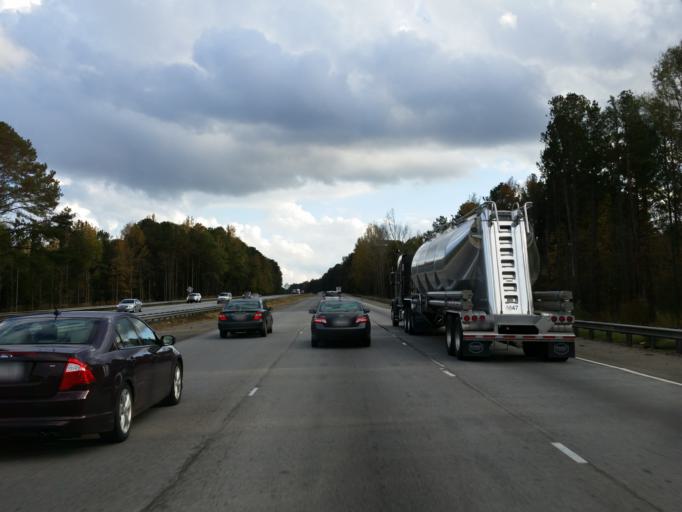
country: US
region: Georgia
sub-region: Henry County
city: Locust Grove
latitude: 33.2364
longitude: -84.0813
